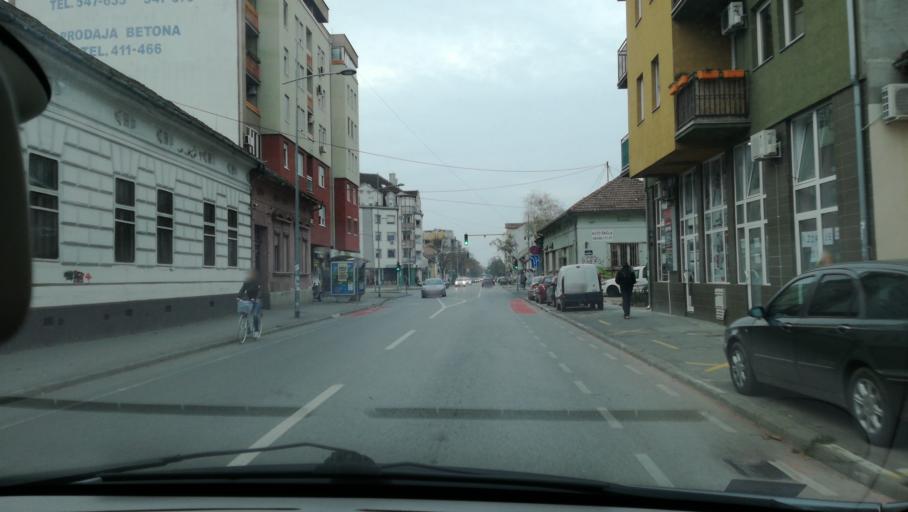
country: RS
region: Autonomna Pokrajina Vojvodina
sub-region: Juznobacki Okrug
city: Novi Sad
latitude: 45.2621
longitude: 19.8405
